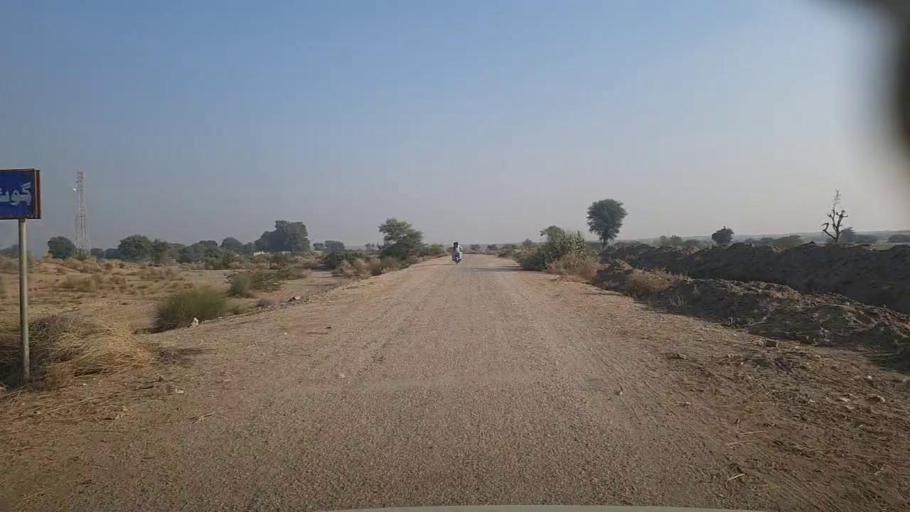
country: PK
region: Sindh
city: Karaundi
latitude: 26.7217
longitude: 68.4923
